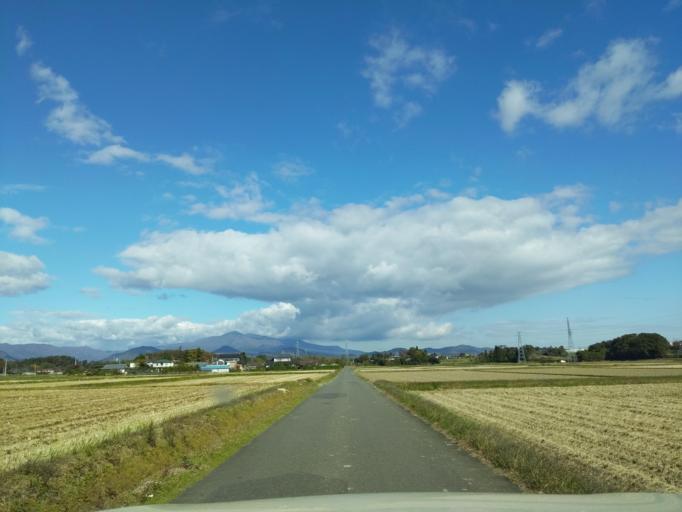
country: JP
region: Fukushima
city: Koriyama
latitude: 37.4233
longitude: 140.3288
